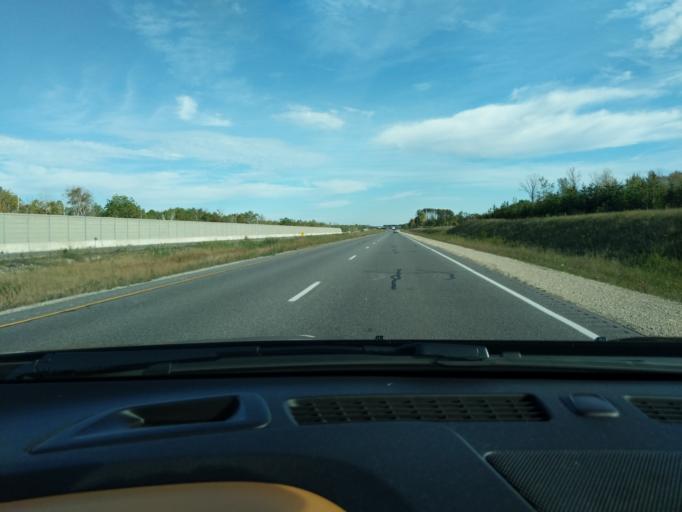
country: CA
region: Ontario
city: Collingwood
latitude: 44.4783
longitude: -80.1608
